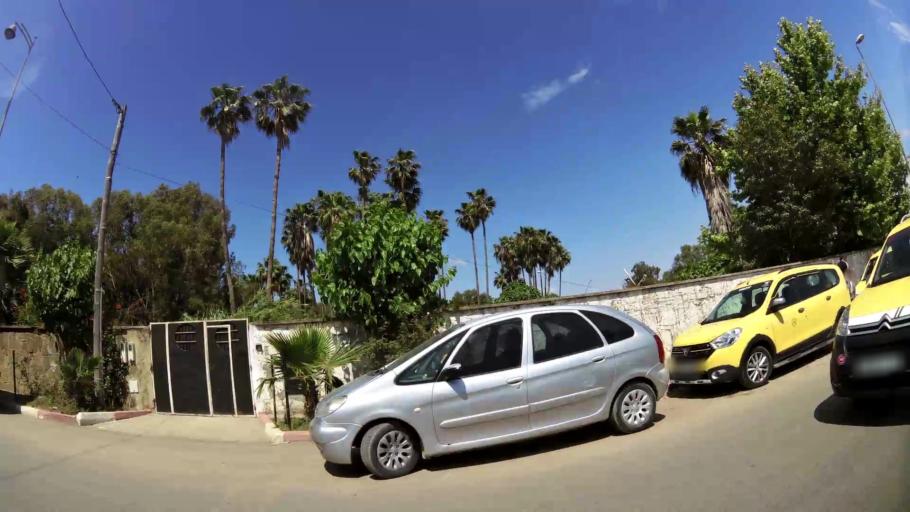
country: MA
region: Gharb-Chrarda-Beni Hssen
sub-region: Kenitra Province
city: Kenitra
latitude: 34.2313
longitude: -6.5341
